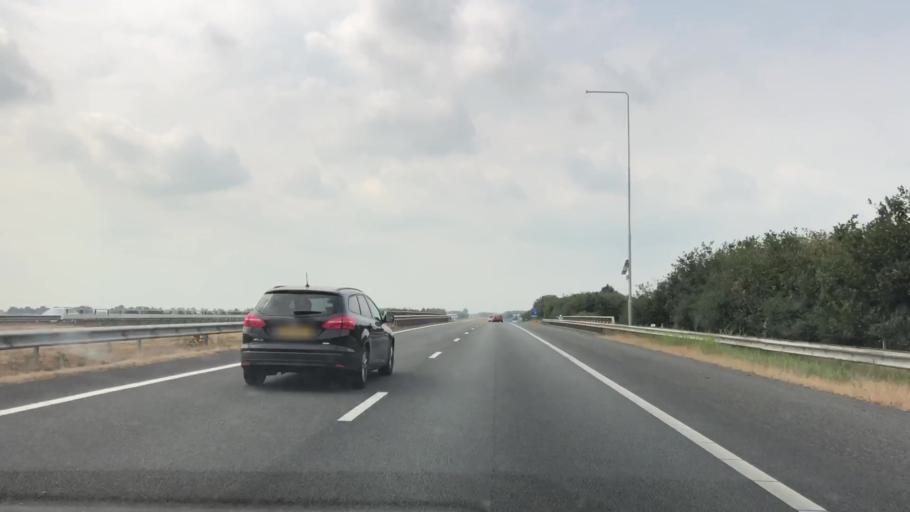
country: NL
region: Drenthe
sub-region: Gemeente Coevorden
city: Dalen
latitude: 52.7207
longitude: 6.6608
